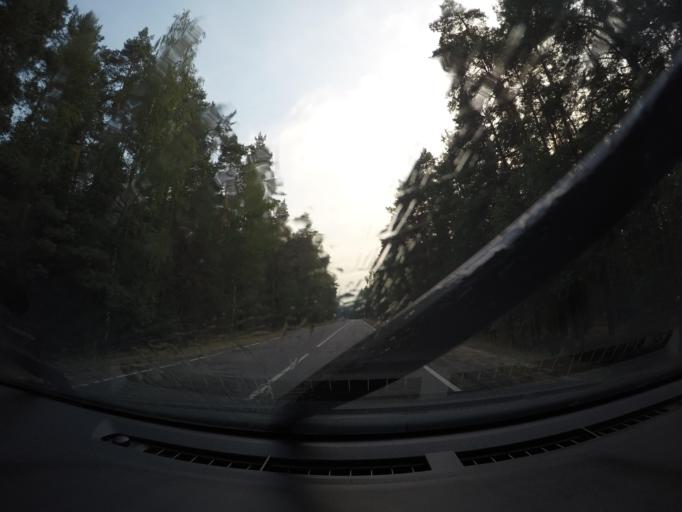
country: RU
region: Moskovskaya
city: Imeni Tsyurupy
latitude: 55.5107
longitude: 38.7192
